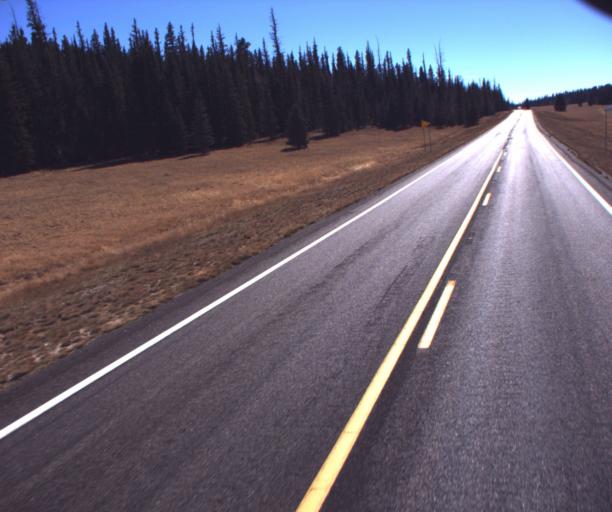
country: US
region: Arizona
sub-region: Coconino County
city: Grand Canyon
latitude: 36.3541
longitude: -112.1183
